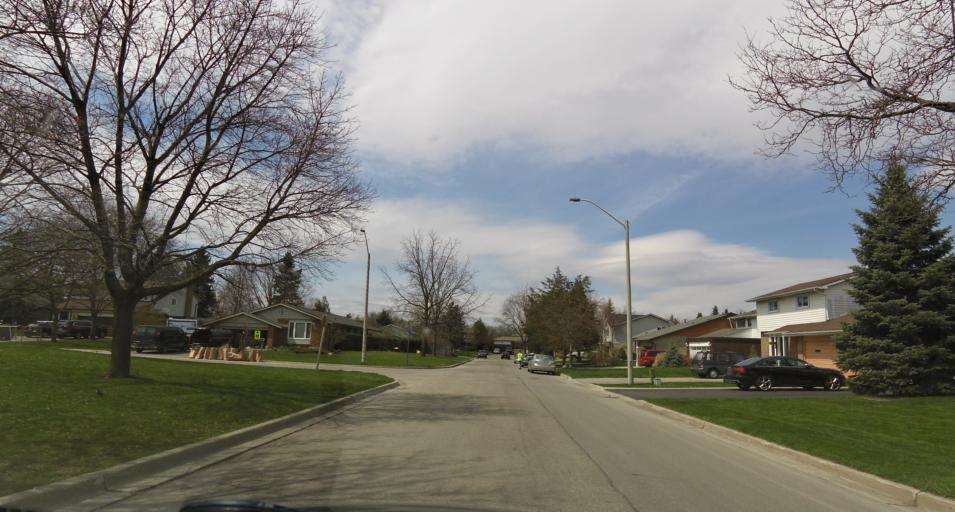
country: CA
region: Ontario
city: Mississauga
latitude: 43.6022
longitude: -79.7212
